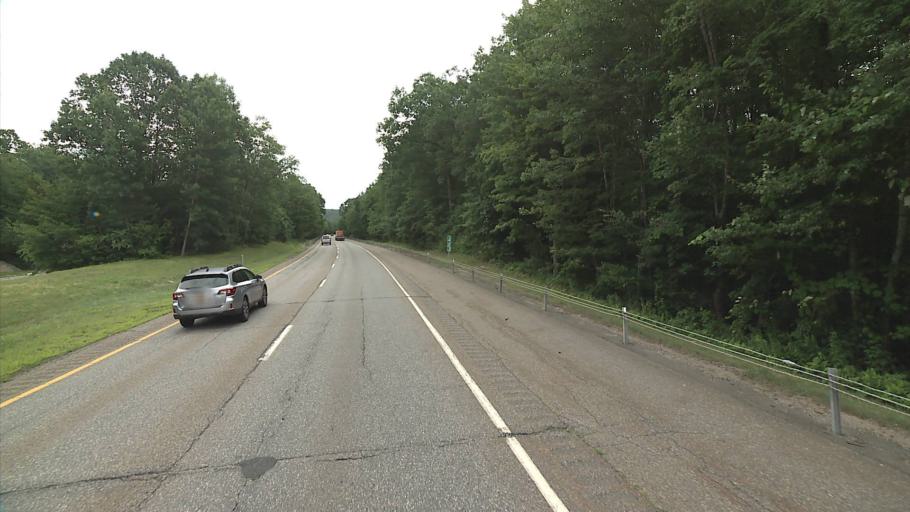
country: US
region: Connecticut
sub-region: Litchfield County
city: Thomaston
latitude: 41.7063
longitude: -73.0790
